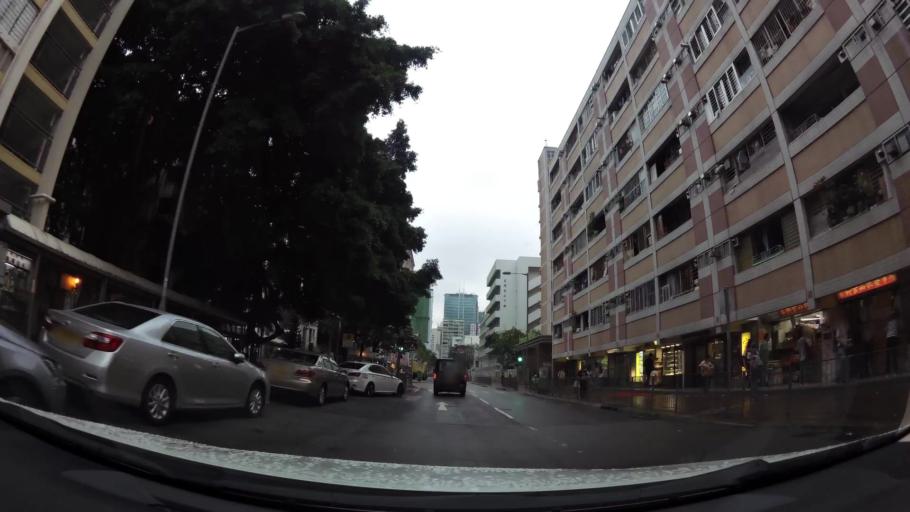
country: HK
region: Tsuen Wan
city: Tsuen Wan
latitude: 22.3736
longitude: 114.1127
